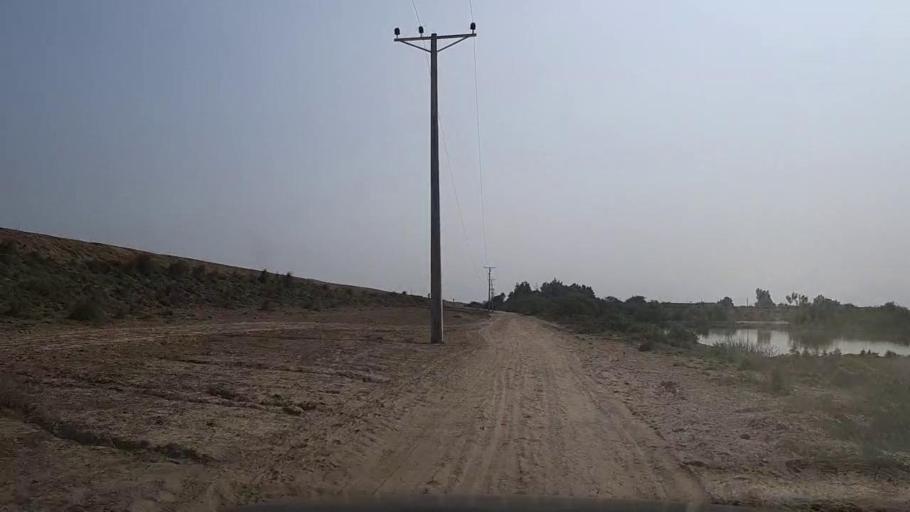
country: PK
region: Sindh
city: Chuhar Jamali
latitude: 24.5547
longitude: 67.9168
